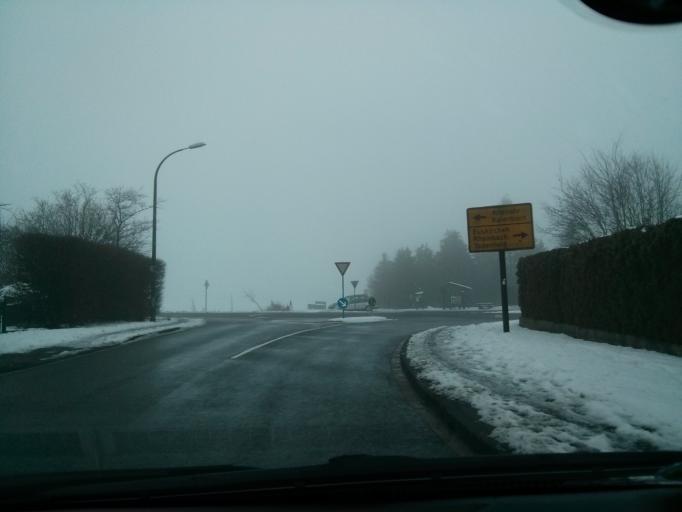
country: DE
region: Rheinland-Pfalz
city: Berg
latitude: 50.5634
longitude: 6.9660
